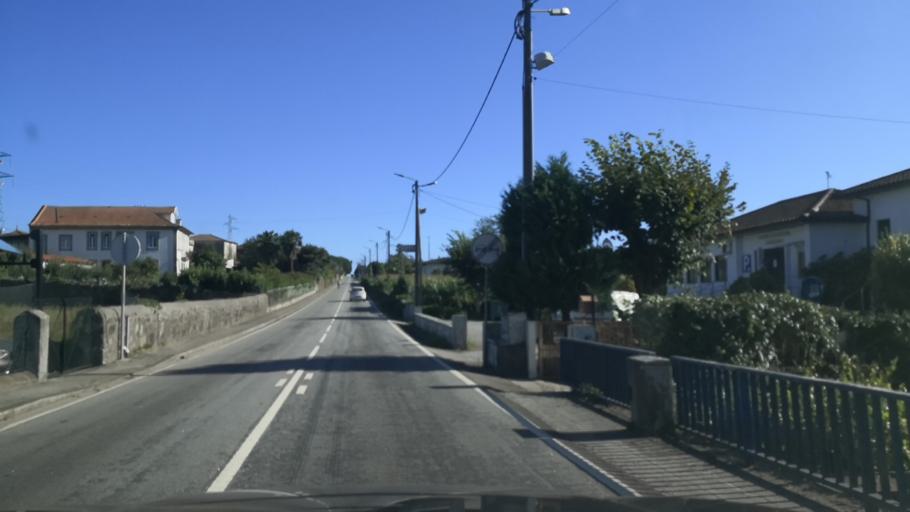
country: PT
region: Porto
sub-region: Santo Tirso
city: Sao Miguel do Couto
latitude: 41.3030
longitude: -8.4710
